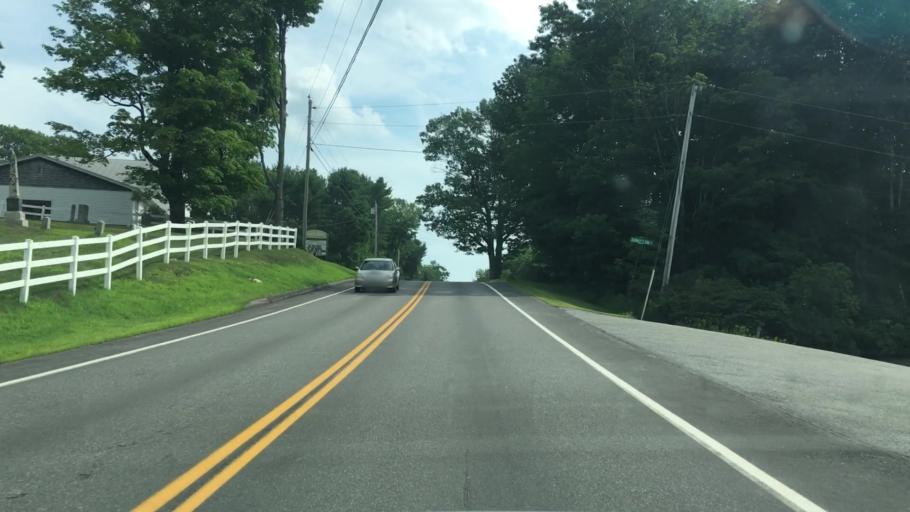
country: US
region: Maine
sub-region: Kennebec County
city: Windsor
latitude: 44.3418
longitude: -69.5820
